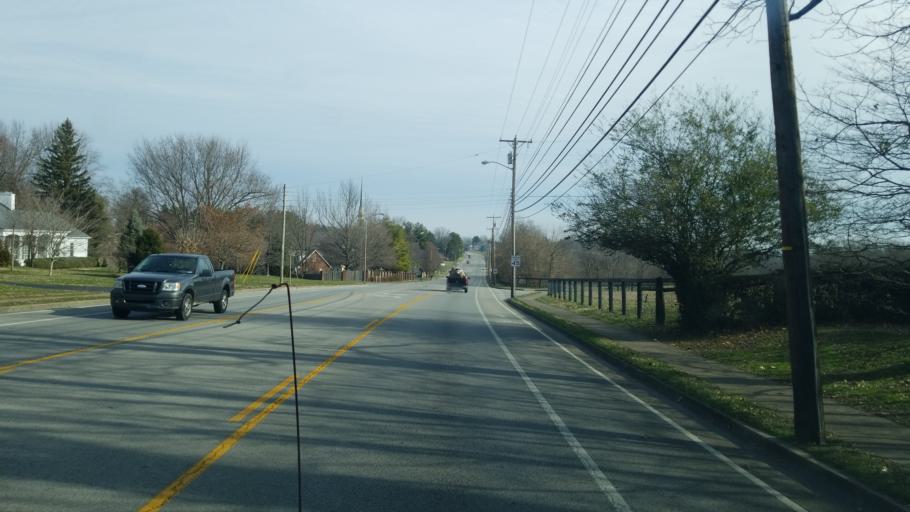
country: US
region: Kentucky
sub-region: Boyle County
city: Danville
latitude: 37.6520
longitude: -84.7592
